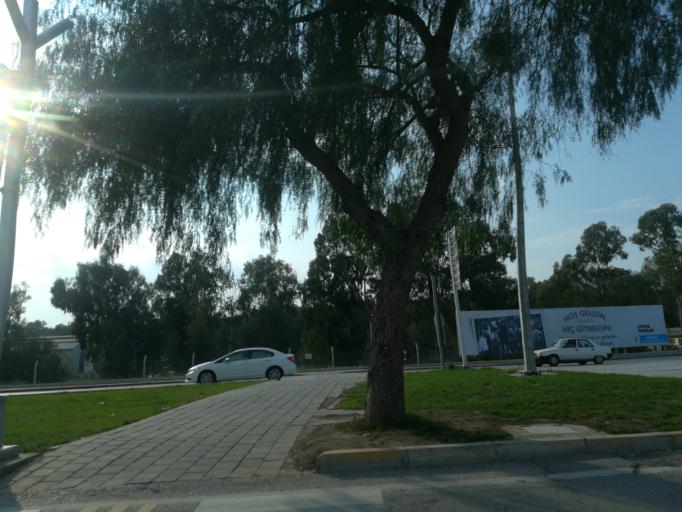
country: TR
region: Adana
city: Adana
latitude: 37.0293
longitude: 35.3453
